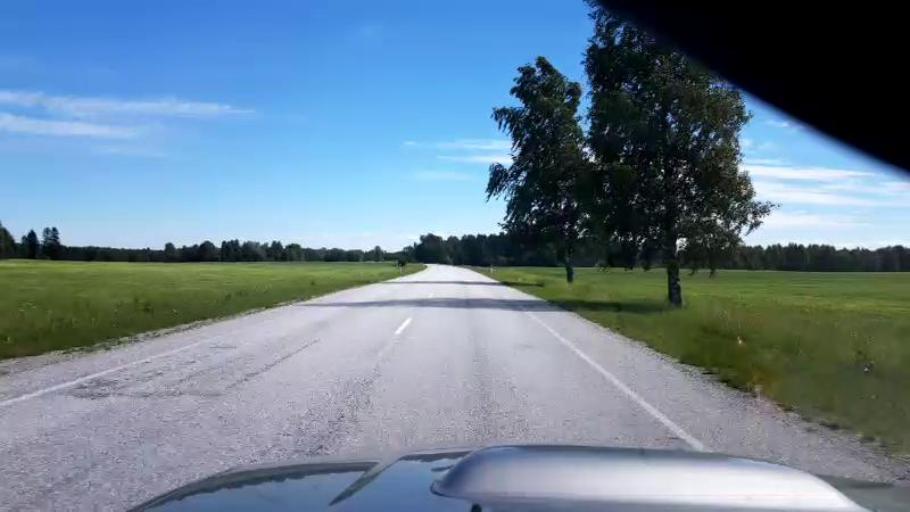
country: EE
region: Laeaene-Virumaa
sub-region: Rakke vald
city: Rakke
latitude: 58.9477
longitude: 26.1841
